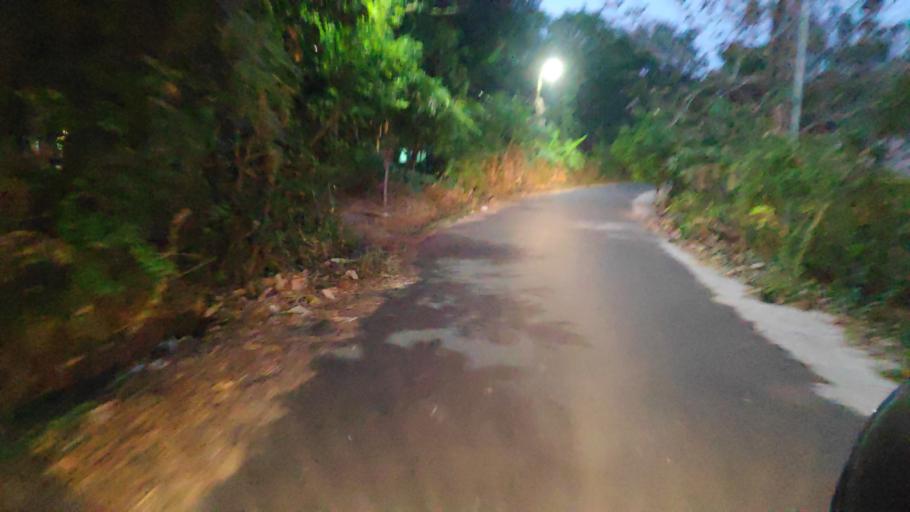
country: IN
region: Kerala
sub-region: Kozhikode
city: Kunnamangalam
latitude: 11.2803
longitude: 75.8365
